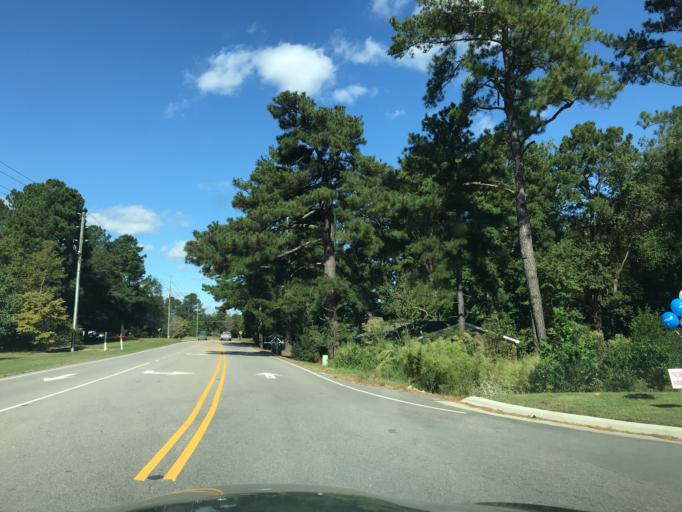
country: US
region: North Carolina
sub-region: Wake County
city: Wake Forest
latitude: 35.9322
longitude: -78.5051
